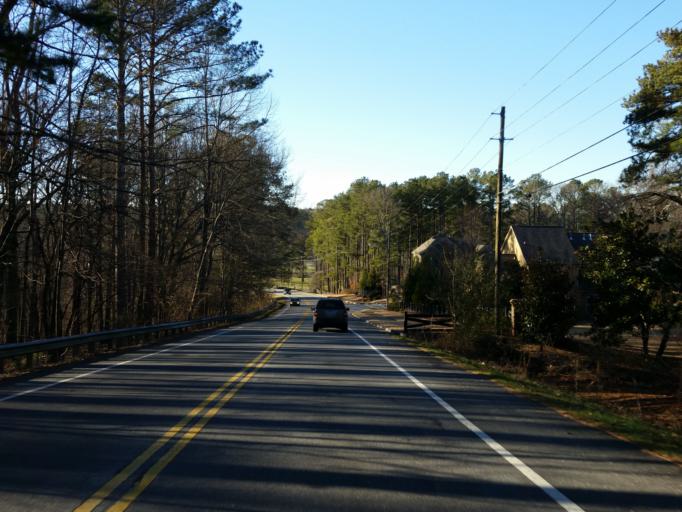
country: US
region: Georgia
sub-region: Cobb County
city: Kennesaw
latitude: 33.9742
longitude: -84.6795
